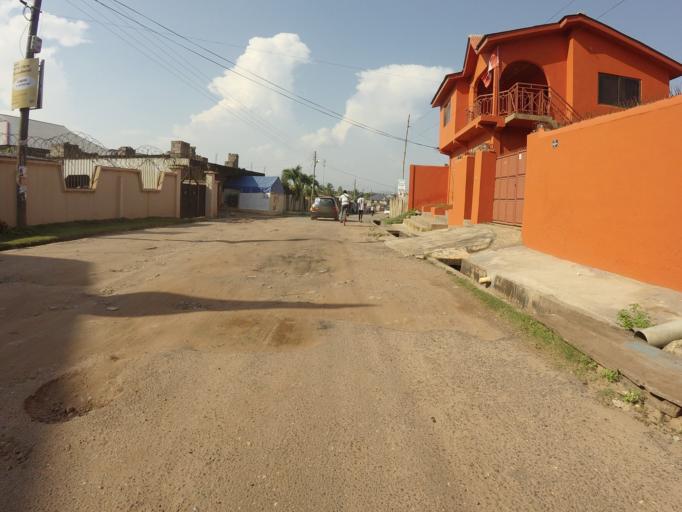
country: GH
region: Greater Accra
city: Dome
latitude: 5.6114
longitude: -0.2439
